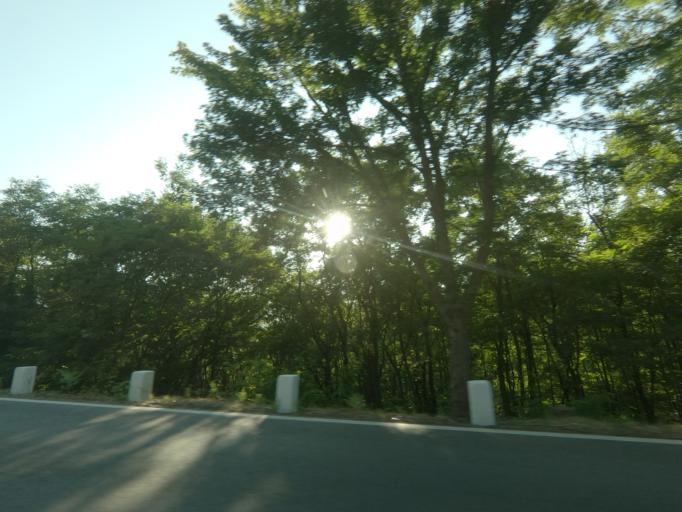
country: PT
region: Vila Real
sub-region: Vila Real
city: Vila Real
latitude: 41.2948
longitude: -7.7093
